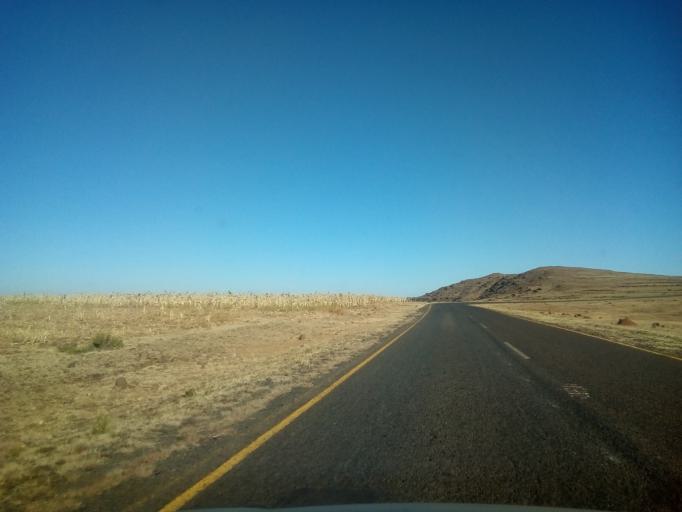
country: LS
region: Berea
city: Teyateyaneng
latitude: -29.2543
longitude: 27.7768
